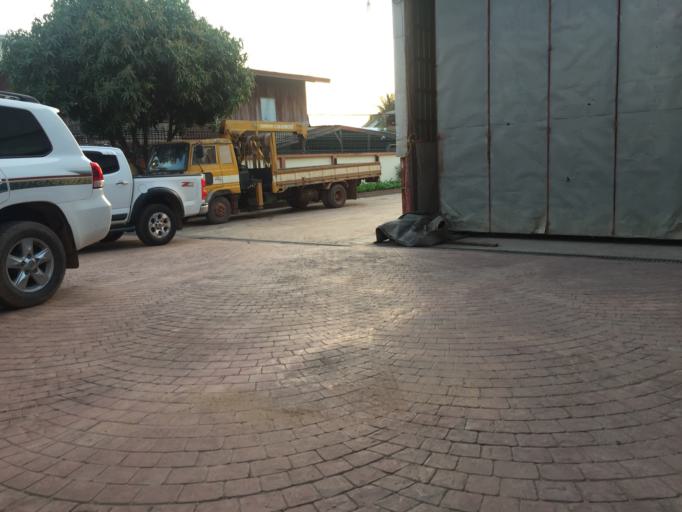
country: LA
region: Vientiane
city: Vientiane
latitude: 17.9800
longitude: 102.6016
